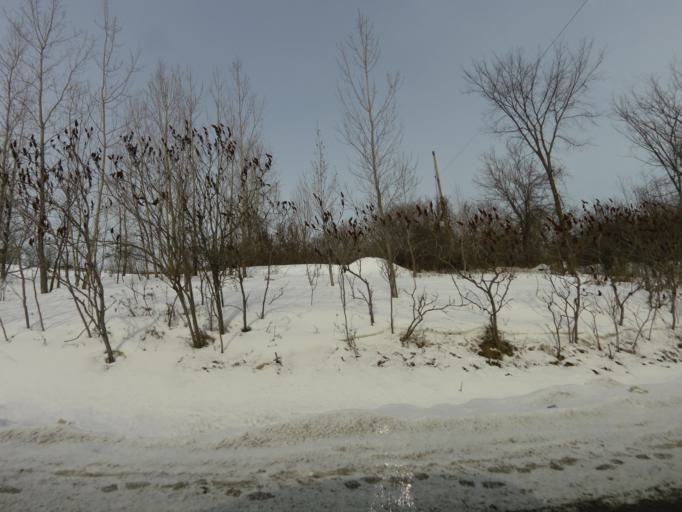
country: CA
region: Quebec
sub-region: Outaouais
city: Gatineau
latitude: 45.4986
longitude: -75.6233
